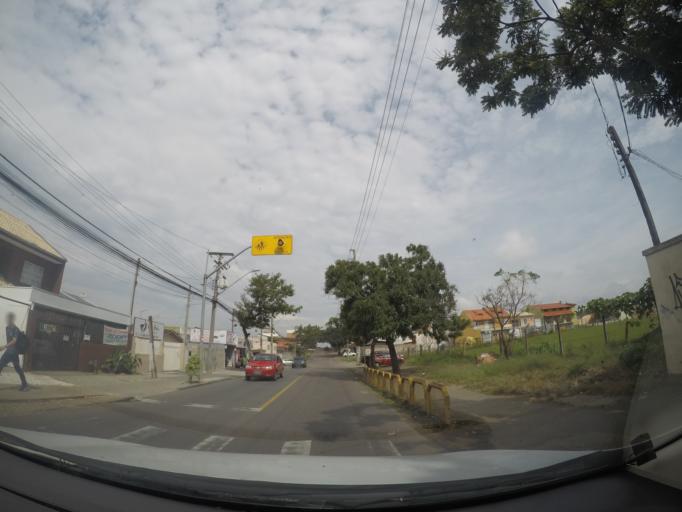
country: BR
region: Parana
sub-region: Sao Jose Dos Pinhais
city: Sao Jose dos Pinhais
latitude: -25.5179
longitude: -49.2768
